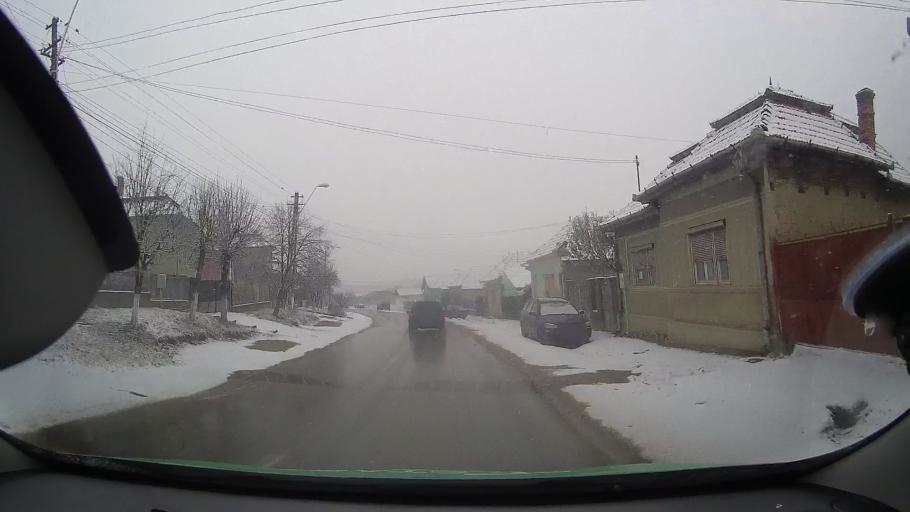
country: RO
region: Alba
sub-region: Municipiul Aiud
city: Aiudul de Sus
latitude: 46.3125
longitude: 23.6989
